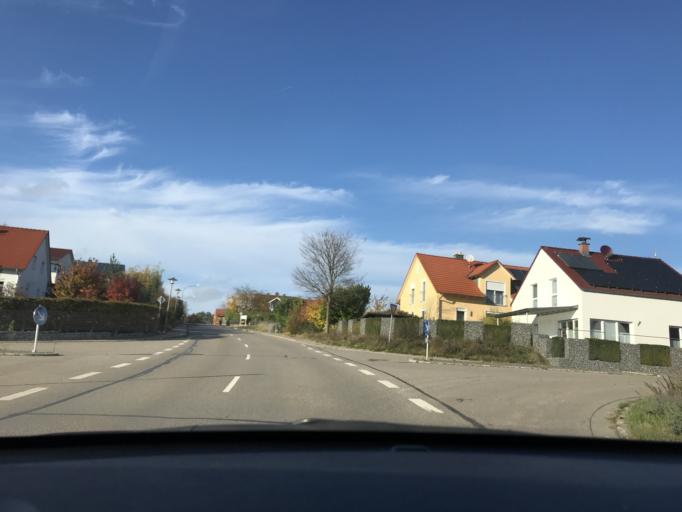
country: DE
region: Bavaria
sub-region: Upper Palatinate
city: Pentling
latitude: 48.9590
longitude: 12.0807
